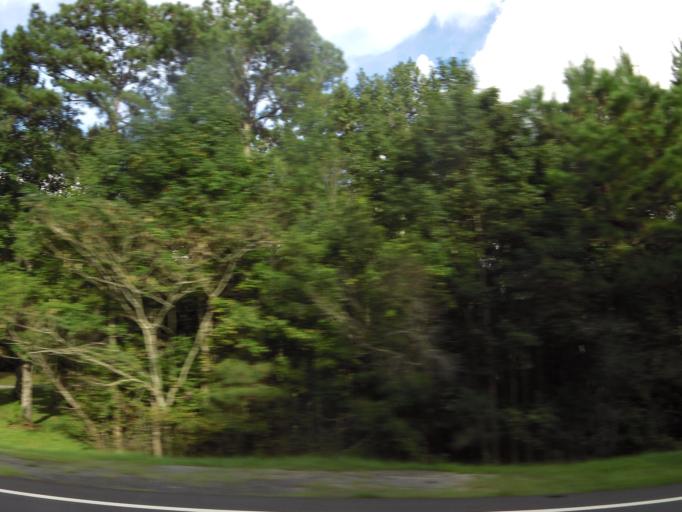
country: US
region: Georgia
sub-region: Liberty County
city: Midway
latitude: 31.8138
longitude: -81.4302
